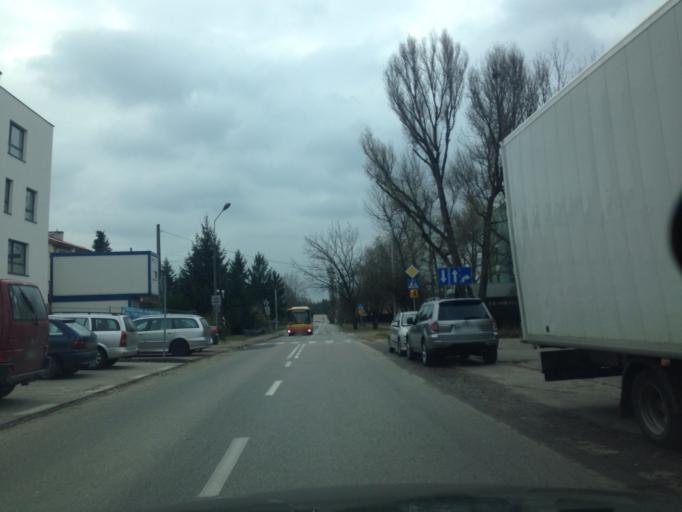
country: PL
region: Masovian Voivodeship
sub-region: Warszawa
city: Rembertow
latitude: 52.2599
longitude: 21.1782
